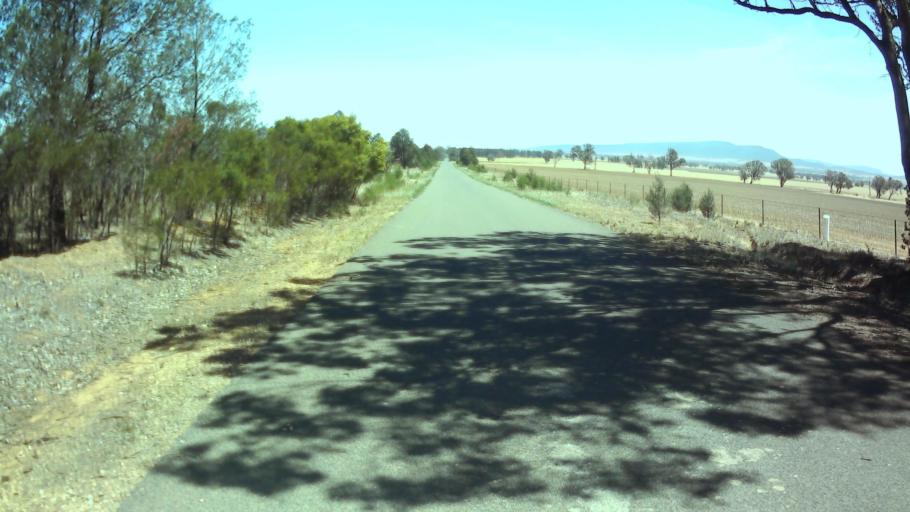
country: AU
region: New South Wales
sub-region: Weddin
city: Grenfell
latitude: -34.0534
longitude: 148.2199
